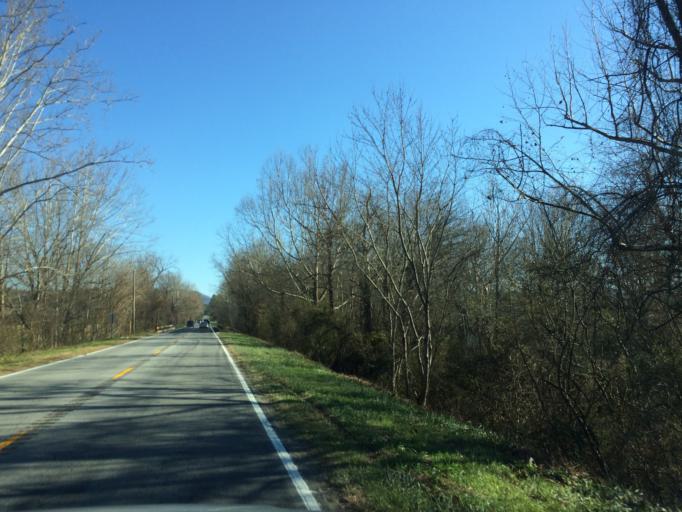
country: US
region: North Carolina
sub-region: Henderson County
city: Mills River
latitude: 35.3735
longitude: -82.5373
